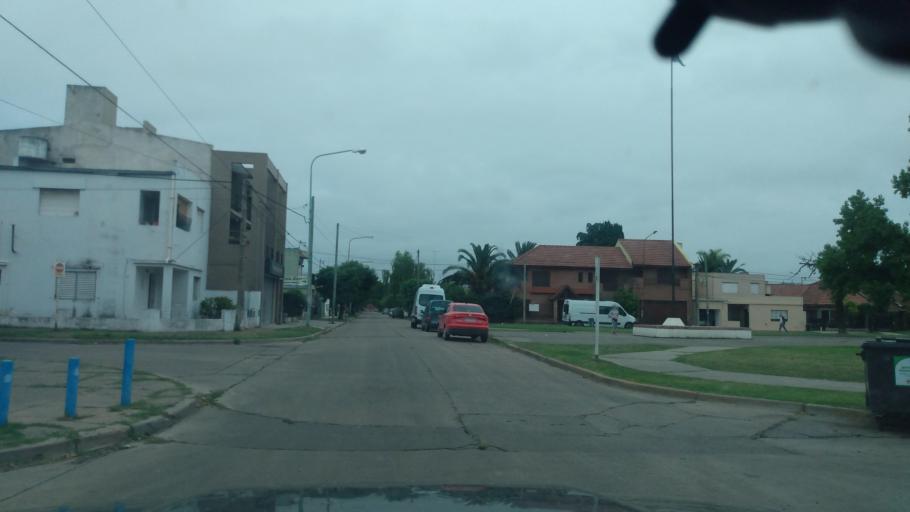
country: AR
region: Buenos Aires
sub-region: Partido de Lujan
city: Lujan
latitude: -34.5717
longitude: -59.1165
